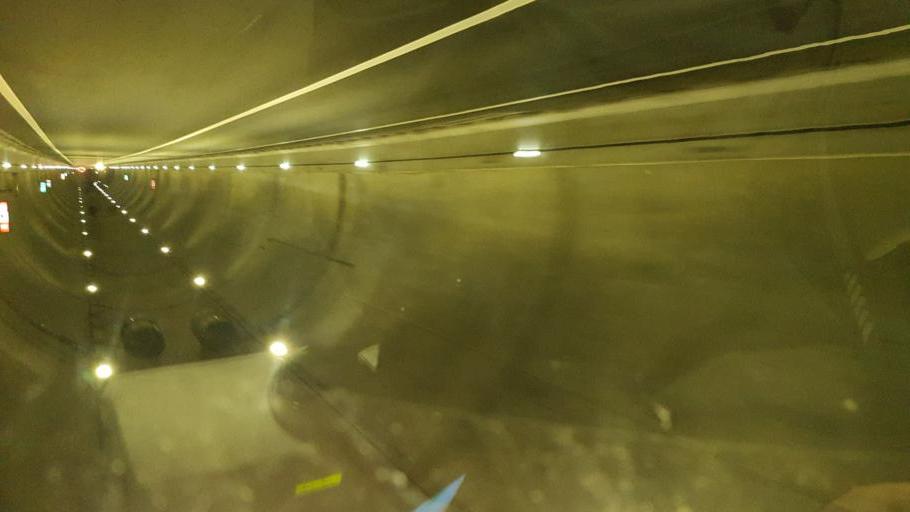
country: IT
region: Liguria
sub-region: Provincia di Genova
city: San Teodoro
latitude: 44.4258
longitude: 8.8672
